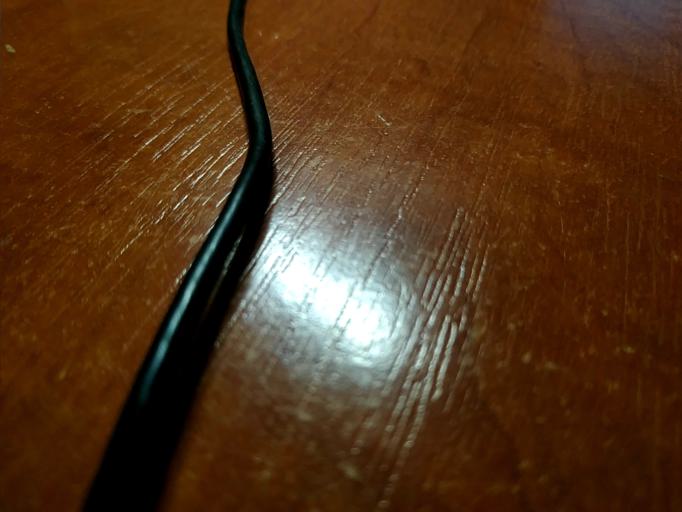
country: RU
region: Arkhangelskaya
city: Onega
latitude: 63.7628
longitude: 38.0745
